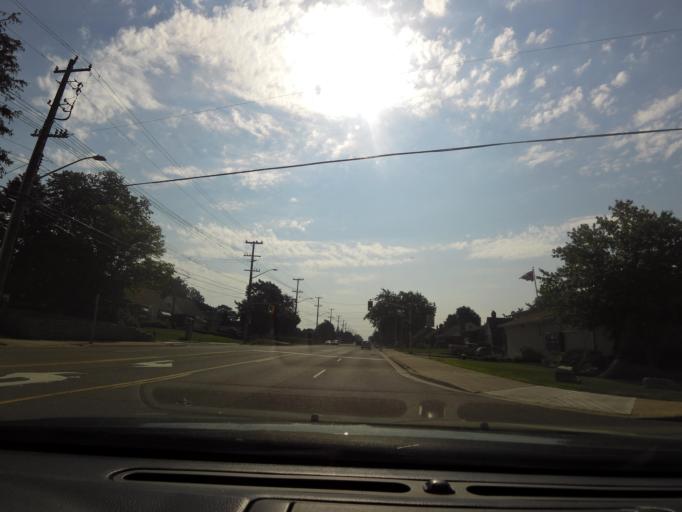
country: CA
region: Ontario
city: Hamilton
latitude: 43.2282
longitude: -79.8794
